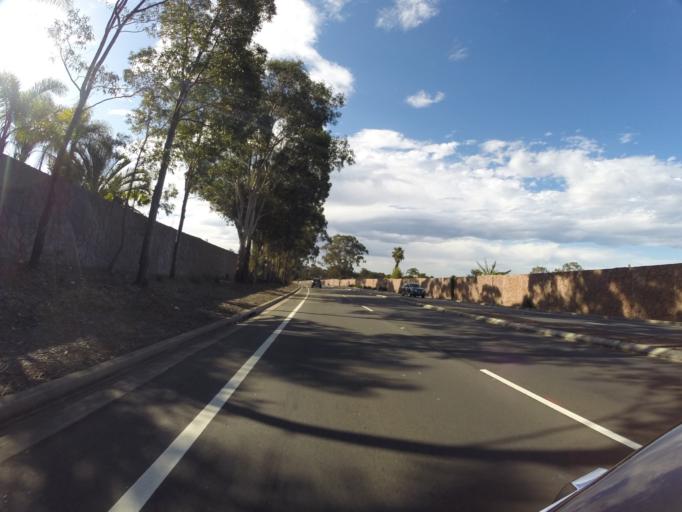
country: AU
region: New South Wales
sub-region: Fairfield
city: Cecil Park
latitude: -33.8753
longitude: 150.8690
